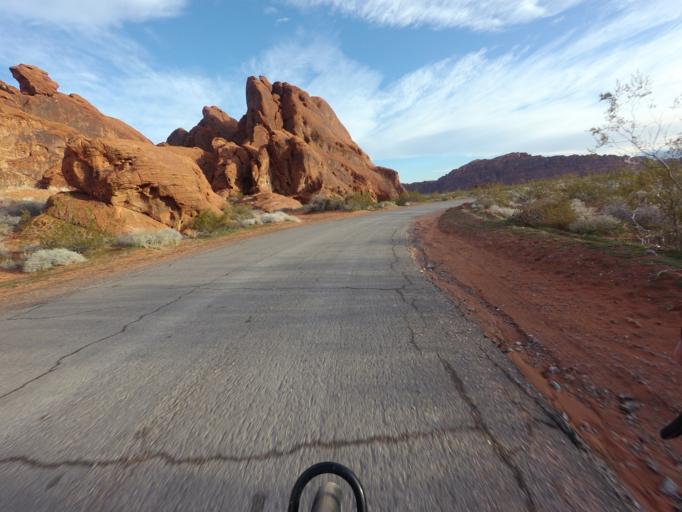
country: US
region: Nevada
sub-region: Clark County
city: Moapa Valley
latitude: 36.4192
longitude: -114.5517
